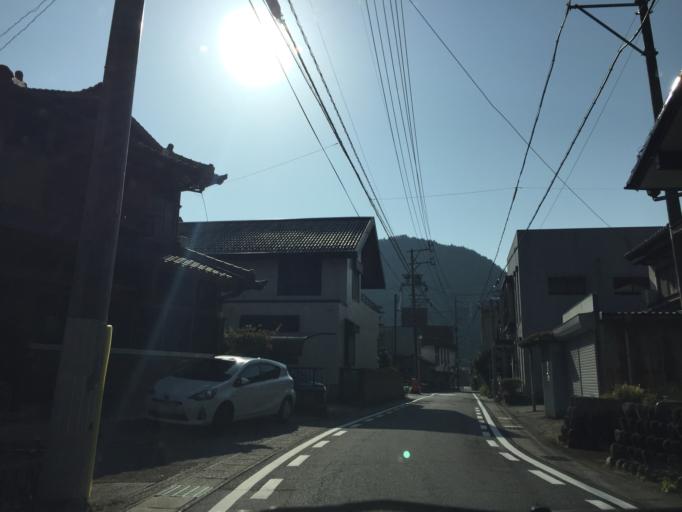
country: JP
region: Gifu
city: Minokamo
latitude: 35.5445
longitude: 137.1206
